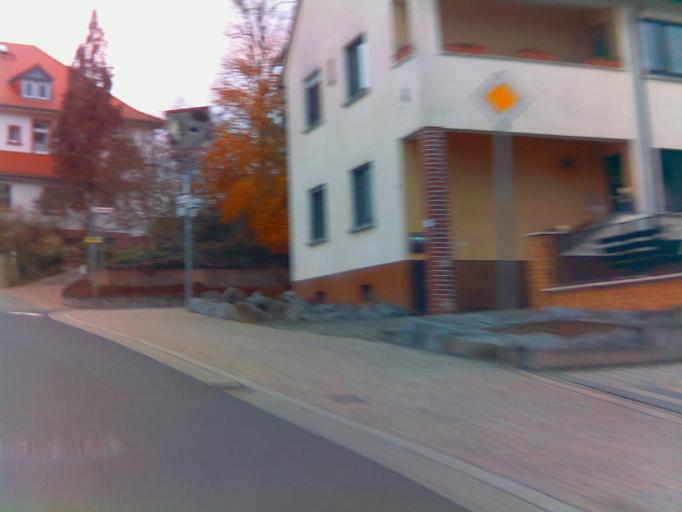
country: DE
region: Hesse
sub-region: Regierungsbezirk Darmstadt
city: Schaafheim
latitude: 49.8914
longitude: 9.0269
